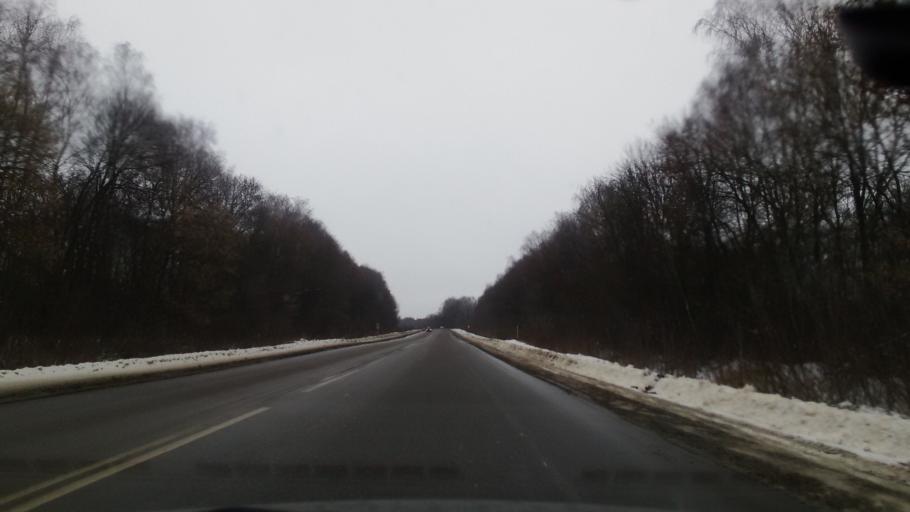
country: RU
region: Tula
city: Bolokhovo
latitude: 54.0477
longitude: 37.8491
